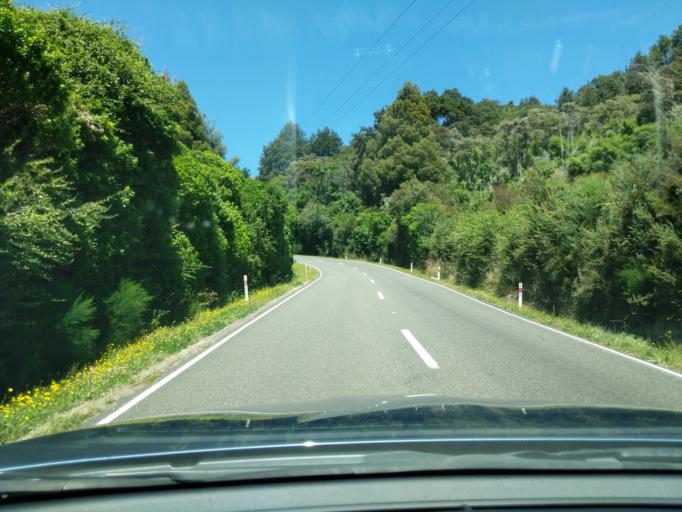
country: NZ
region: Tasman
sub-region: Tasman District
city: Takaka
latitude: -40.7248
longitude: 172.6039
